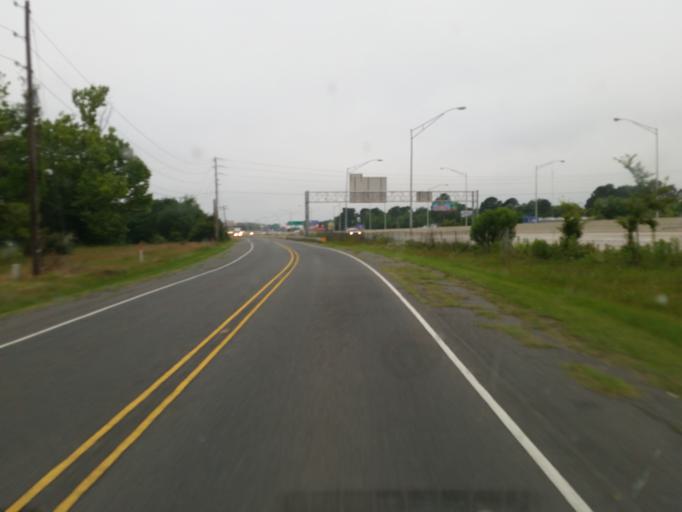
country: US
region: Louisiana
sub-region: Caddo Parish
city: Greenwood
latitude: 32.4534
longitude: -93.8515
